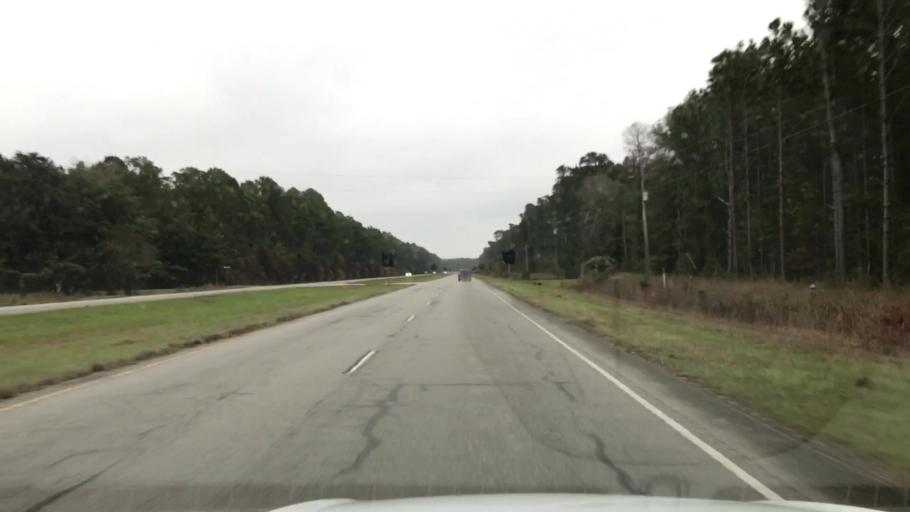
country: US
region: South Carolina
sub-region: Charleston County
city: Awendaw
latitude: 33.0452
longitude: -79.5807
